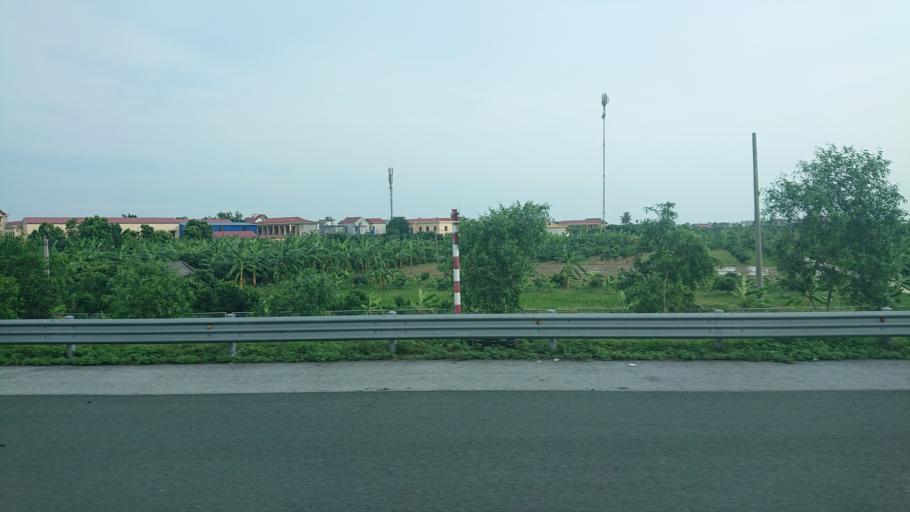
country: VN
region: Hai Phong
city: An Lao
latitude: 20.8141
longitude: 106.4961
